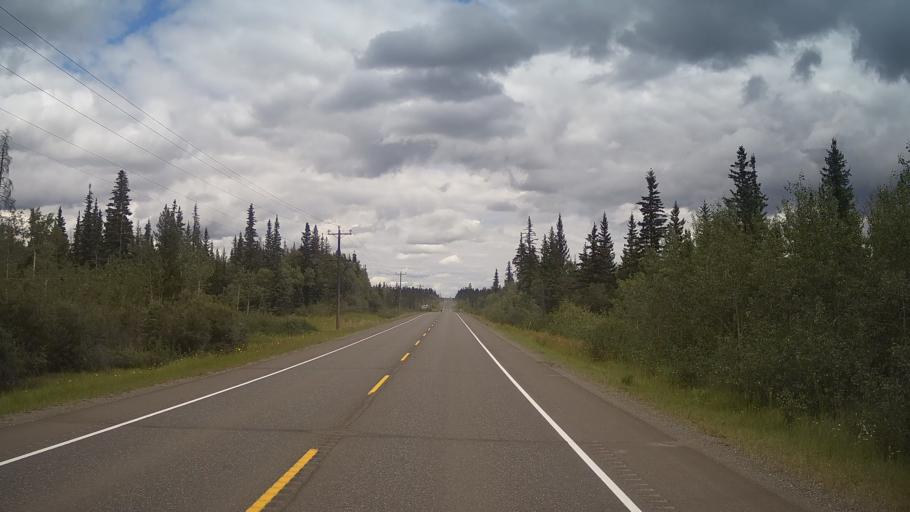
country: CA
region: British Columbia
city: Cache Creek
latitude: 51.2175
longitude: -121.5213
